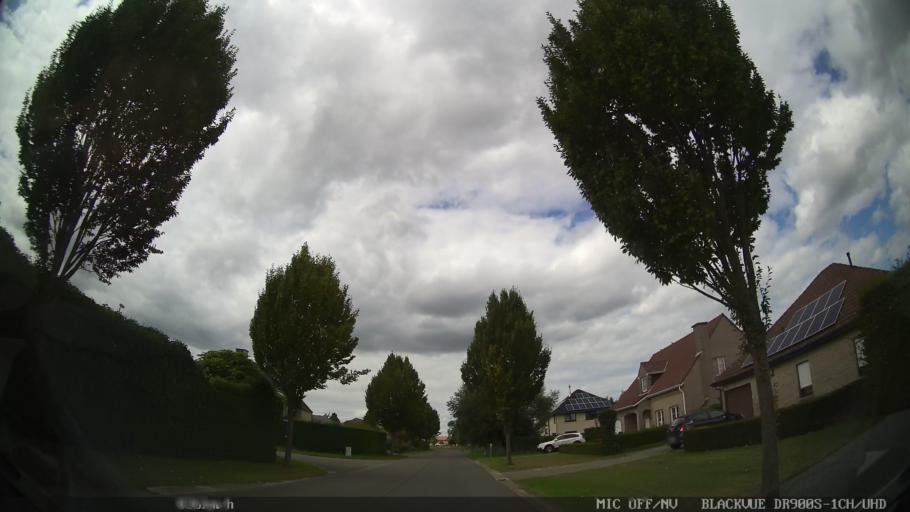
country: BE
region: Flanders
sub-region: Provincie Antwerpen
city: Stabroek
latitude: 51.3342
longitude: 4.3821
